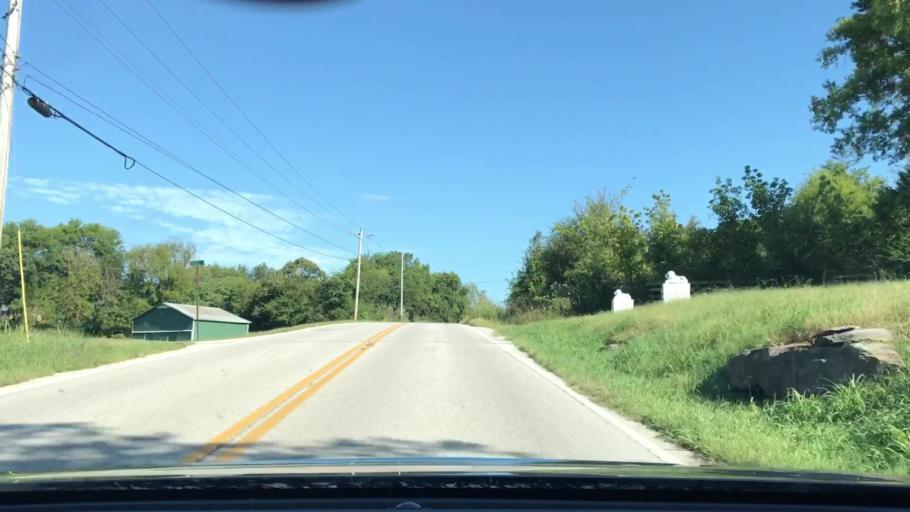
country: US
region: Tennessee
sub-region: Smith County
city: Carthage
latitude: 36.3240
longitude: -85.9071
